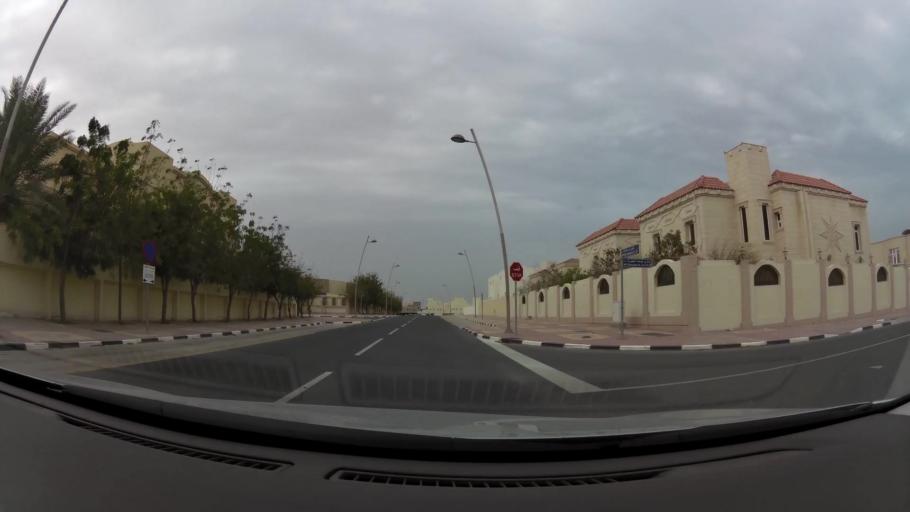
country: QA
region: Baladiyat ad Dawhah
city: Doha
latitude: 25.3361
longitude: 51.4906
